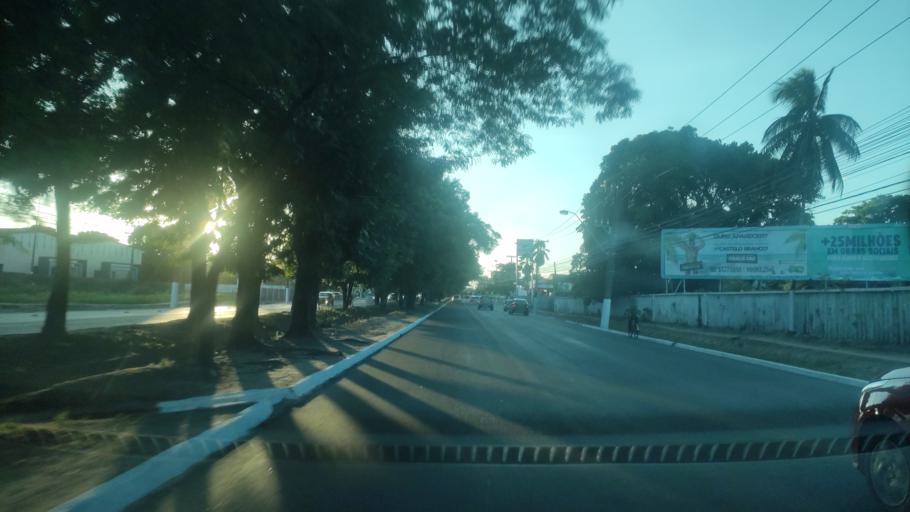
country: BR
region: Alagoas
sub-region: Maceio
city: Maceio
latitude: -9.5940
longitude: -35.7536
